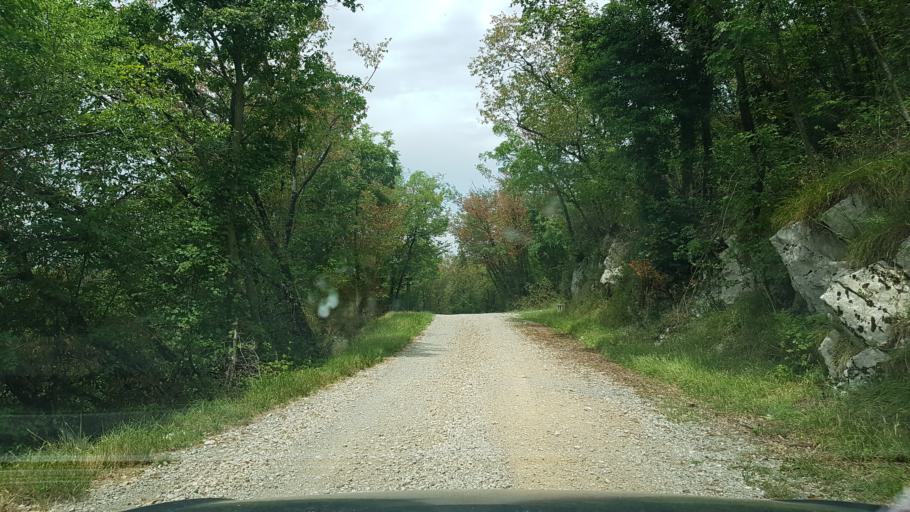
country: SI
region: Kanal
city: Deskle
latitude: 46.0169
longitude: 13.6200
